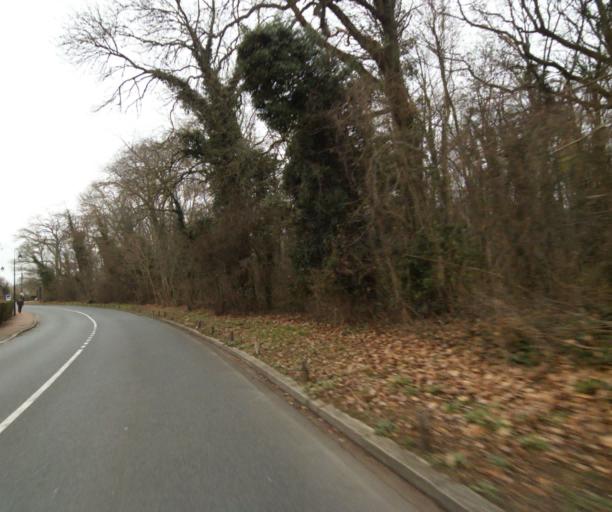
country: FR
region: Ile-de-France
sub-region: Departement des Hauts-de-Seine
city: Garches
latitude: 48.8480
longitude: 2.1698
